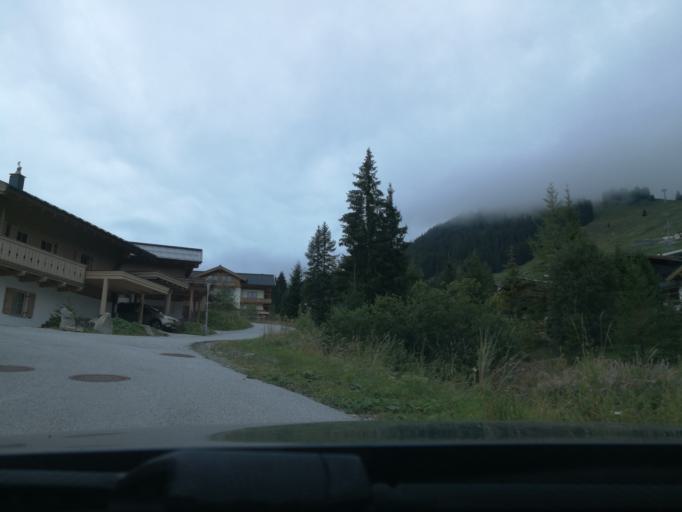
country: AT
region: Salzburg
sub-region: Politischer Bezirk Zell am See
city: Krimml
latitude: 47.2492
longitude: 12.1256
